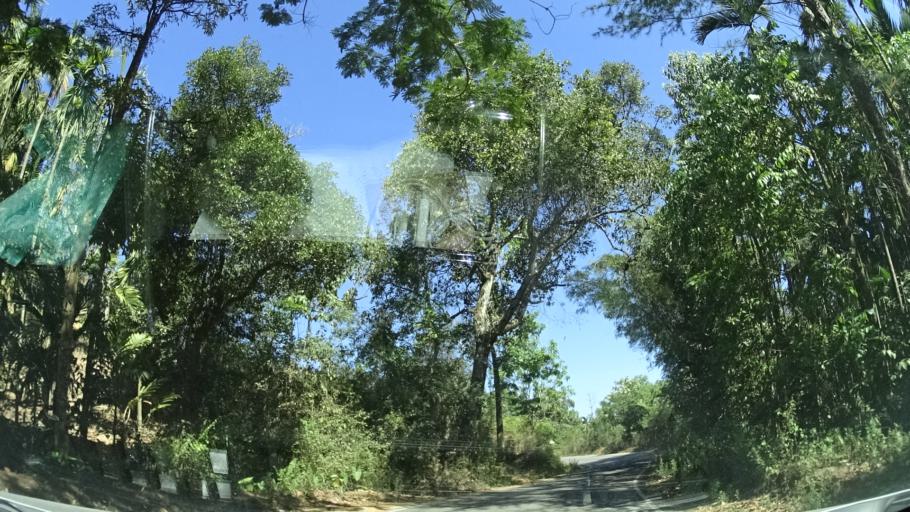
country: IN
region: Karnataka
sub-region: Chikmagalur
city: Sringeri
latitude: 13.2276
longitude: 75.3550
